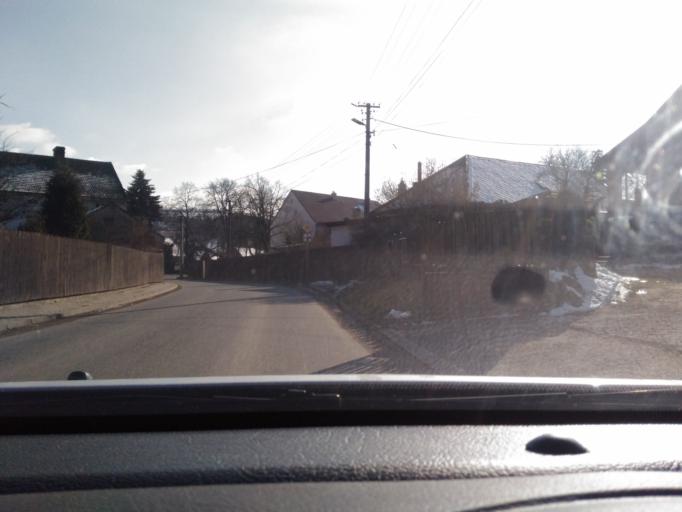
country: CZ
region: South Moravian
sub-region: Okres Brno-Venkov
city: Nedvedice
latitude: 49.5059
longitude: 16.3395
